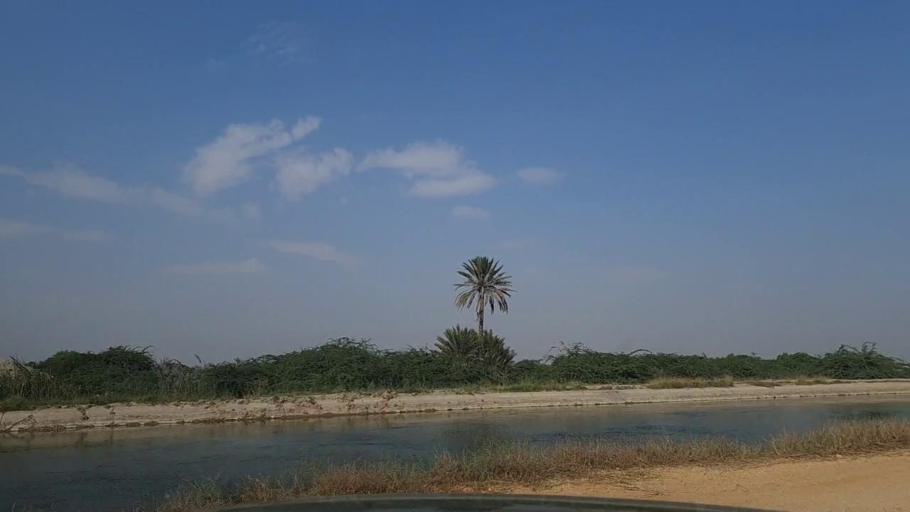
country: PK
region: Sindh
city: Thatta
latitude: 24.8025
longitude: 67.8292
